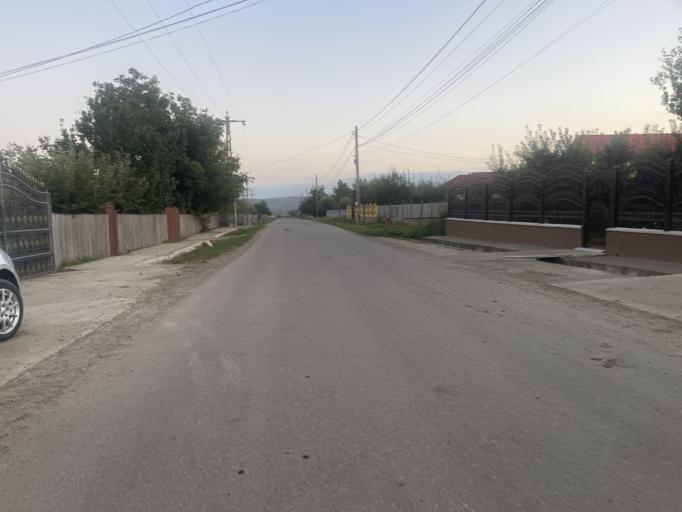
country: RO
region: Iasi
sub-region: Comuna Dumesti
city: Pausesti
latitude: 47.1512
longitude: 27.3237
